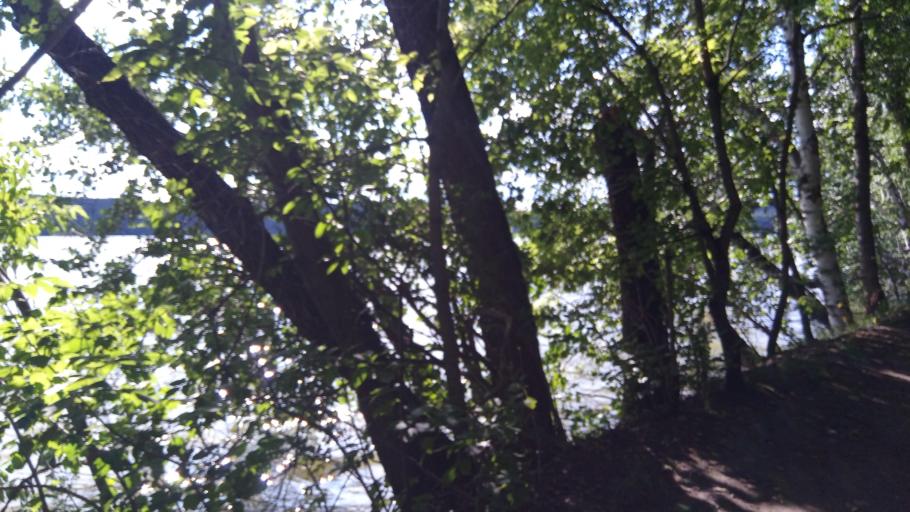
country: RU
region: Chelyabinsk
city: Chebarkul'
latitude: 55.0163
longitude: 60.3127
